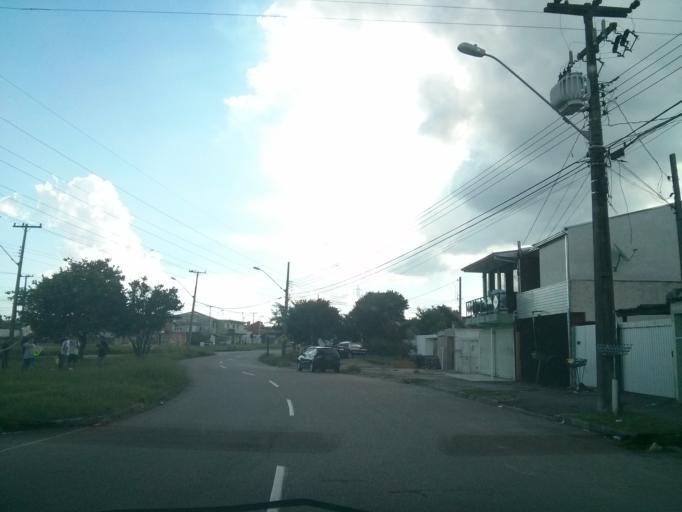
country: BR
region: Parana
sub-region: Sao Jose Dos Pinhais
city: Sao Jose dos Pinhais
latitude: -25.5252
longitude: -49.2318
